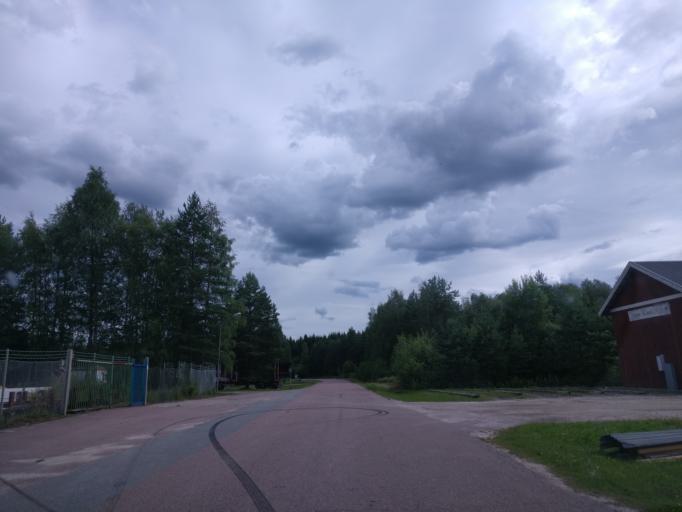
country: SE
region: Vaermland
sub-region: Hagfors Kommun
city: Ekshaerad
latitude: 60.1646
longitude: 13.4978
